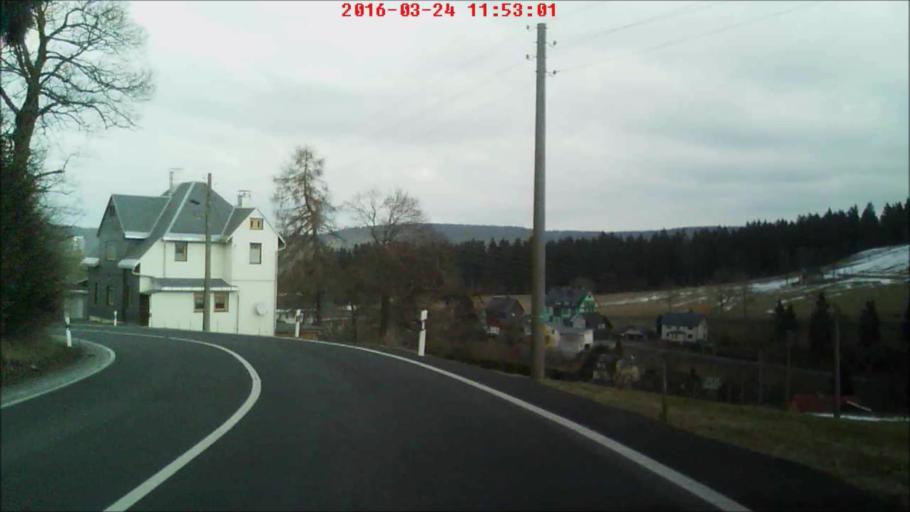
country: DE
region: Thuringia
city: Steinheid
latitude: 50.4709
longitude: 11.0644
